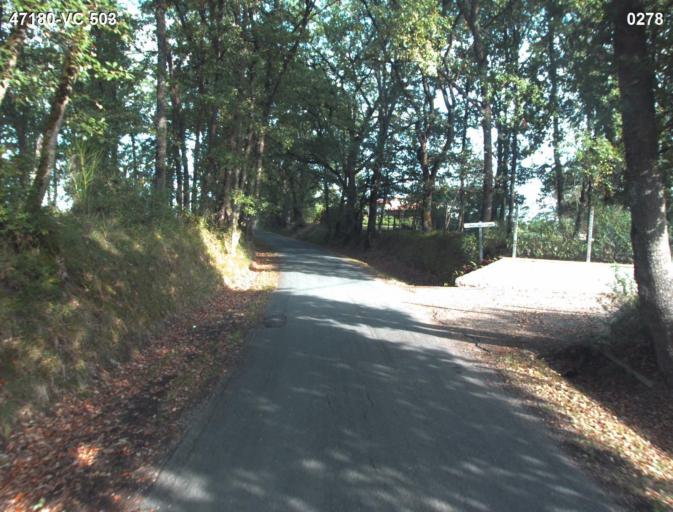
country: FR
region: Aquitaine
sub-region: Departement du Lot-et-Garonne
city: Port-Sainte-Marie
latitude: 44.1809
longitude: 0.4298
